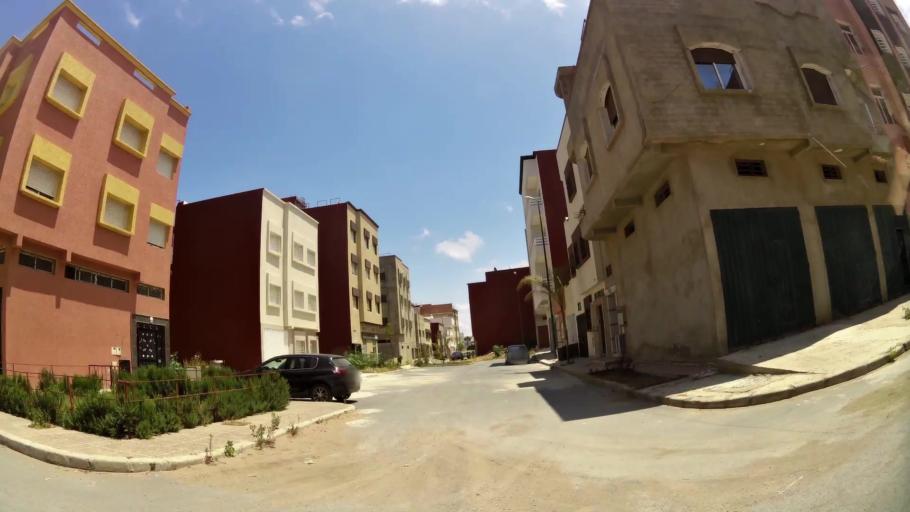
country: MA
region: Gharb-Chrarda-Beni Hssen
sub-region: Kenitra Province
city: Kenitra
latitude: 34.2723
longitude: -6.6185
